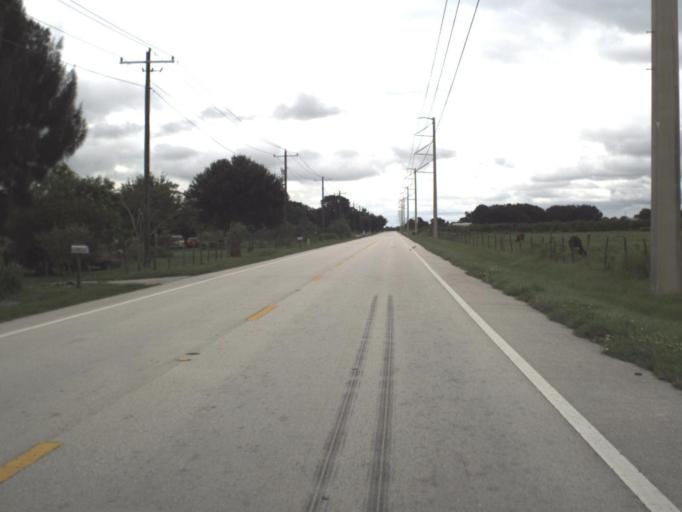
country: US
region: Florida
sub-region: Hardee County
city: Bowling Green
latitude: 27.5948
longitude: -81.8422
